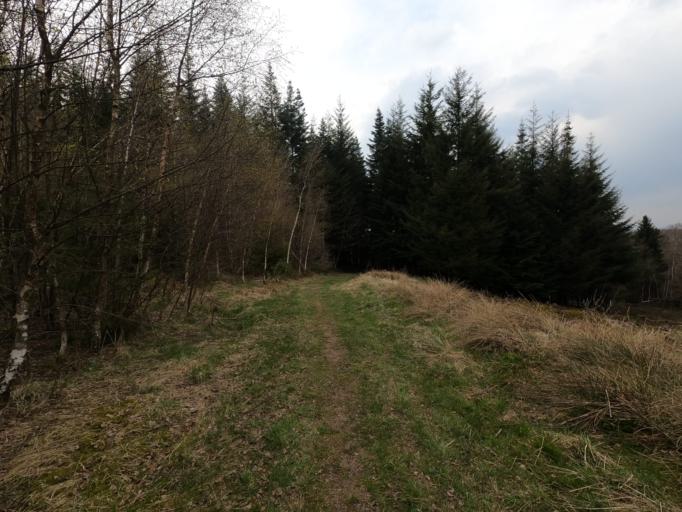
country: DE
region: North Rhine-Westphalia
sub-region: Regierungsbezirk Arnsberg
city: Herscheid
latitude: 51.1642
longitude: 7.7265
